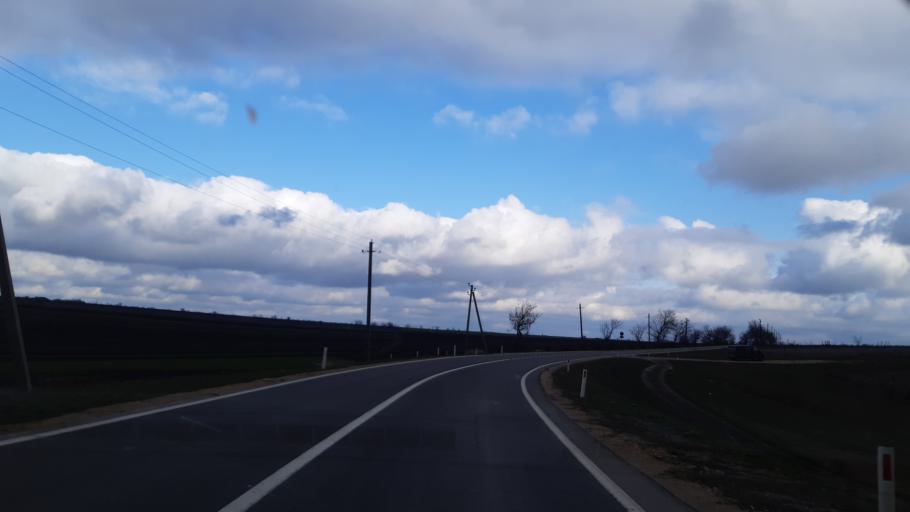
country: MD
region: Chisinau
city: Ciorescu
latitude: 47.2345
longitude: 28.9777
